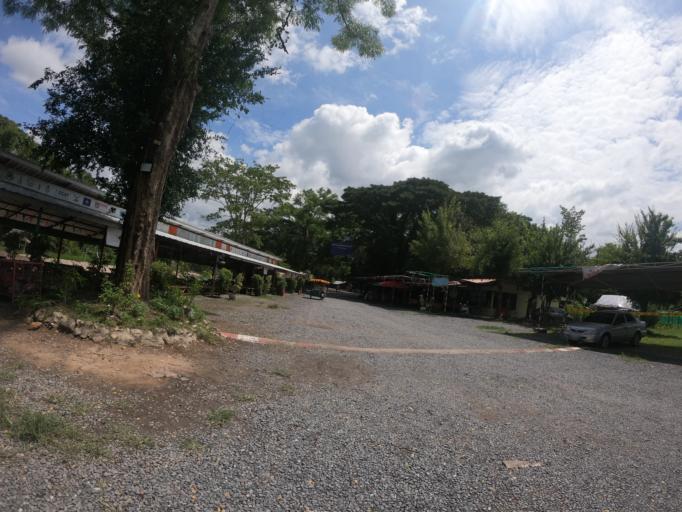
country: TH
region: Nakhon Nayok
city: Nakhon Nayok
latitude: 14.3097
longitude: 101.3129
